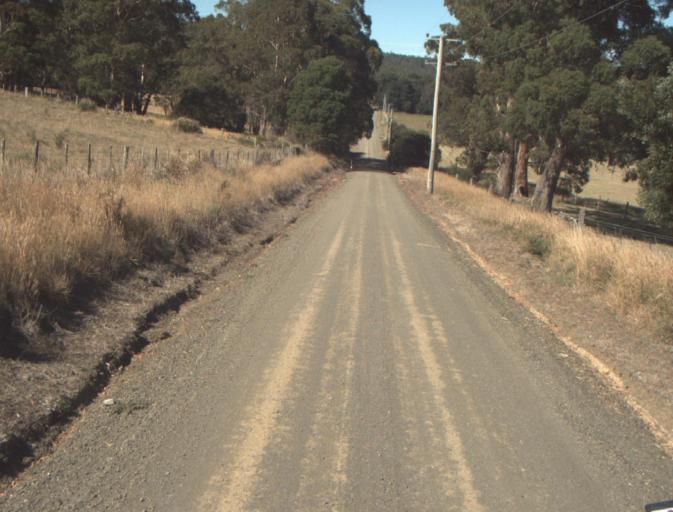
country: AU
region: Tasmania
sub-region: Launceston
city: Newstead
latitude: -41.3133
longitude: 147.3210
